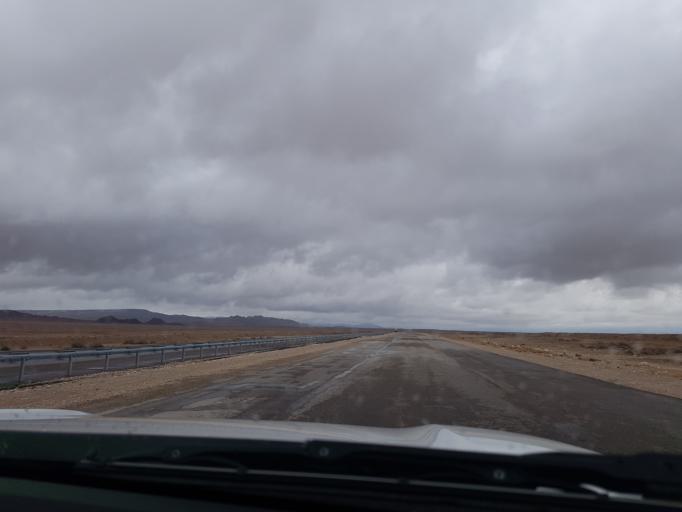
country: TM
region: Balkan
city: Balkanabat
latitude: 39.9122
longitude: 53.8995
